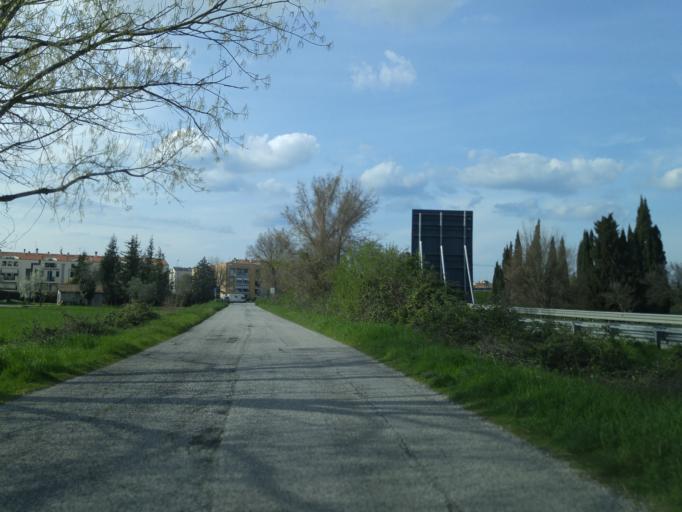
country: IT
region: The Marches
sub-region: Provincia di Pesaro e Urbino
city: Rosciano
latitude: 43.8210
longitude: 13.0144
